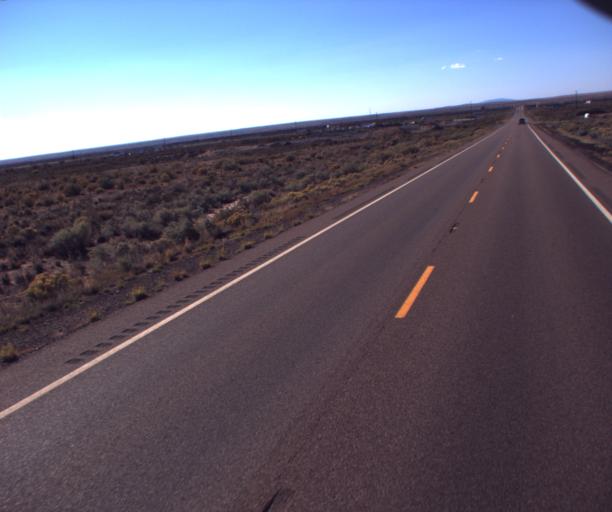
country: US
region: Arizona
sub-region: Navajo County
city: Winslow
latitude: 35.0166
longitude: -110.6361
